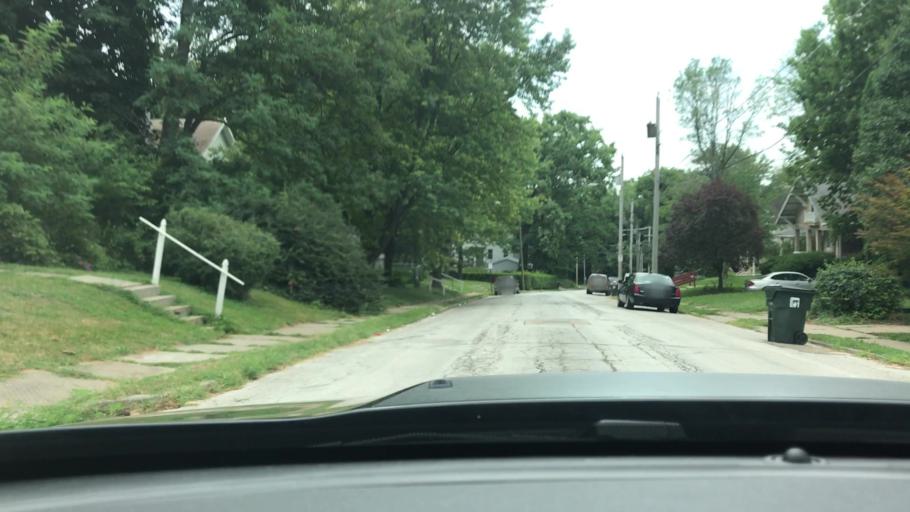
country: US
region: Iowa
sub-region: Scott County
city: Davenport
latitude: 41.5318
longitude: -90.5592
